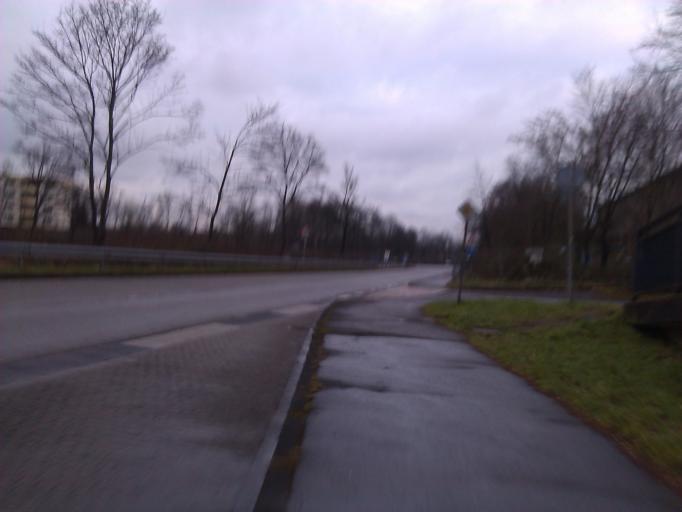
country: DE
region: North Rhine-Westphalia
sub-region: Regierungsbezirk Dusseldorf
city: Essen
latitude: 51.4207
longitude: 6.9834
